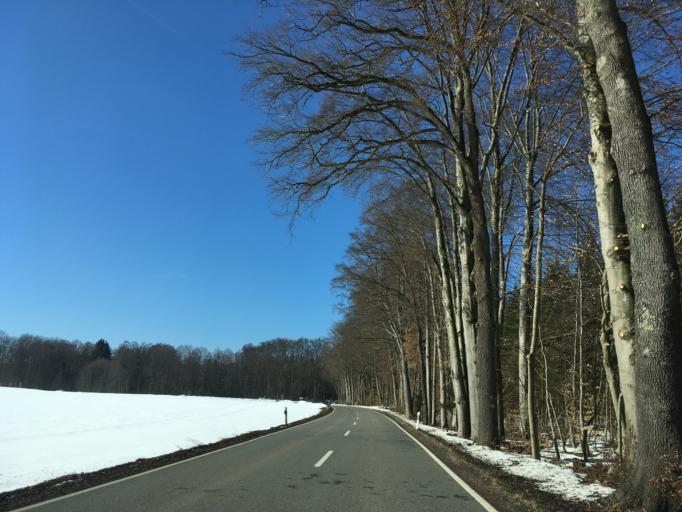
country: DE
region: Bavaria
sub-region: Upper Bavaria
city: Steinhoring
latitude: 48.1287
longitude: 12.0484
